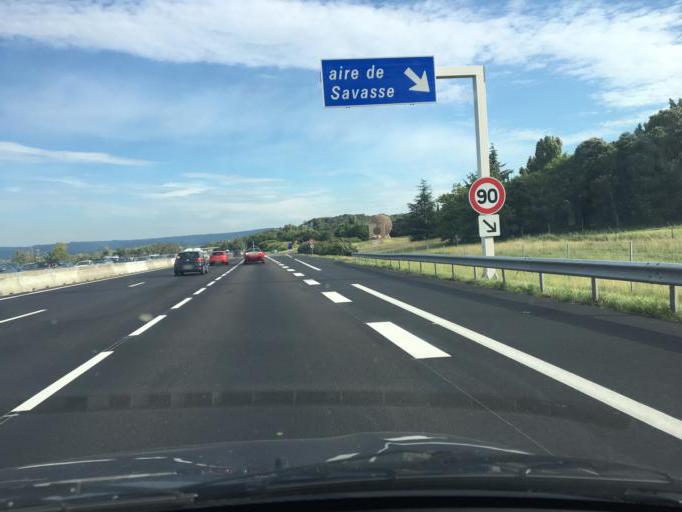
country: FR
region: Rhone-Alpes
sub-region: Departement de la Drome
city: Saint-Marcel-les-Sauzet
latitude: 44.6022
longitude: 4.7946
